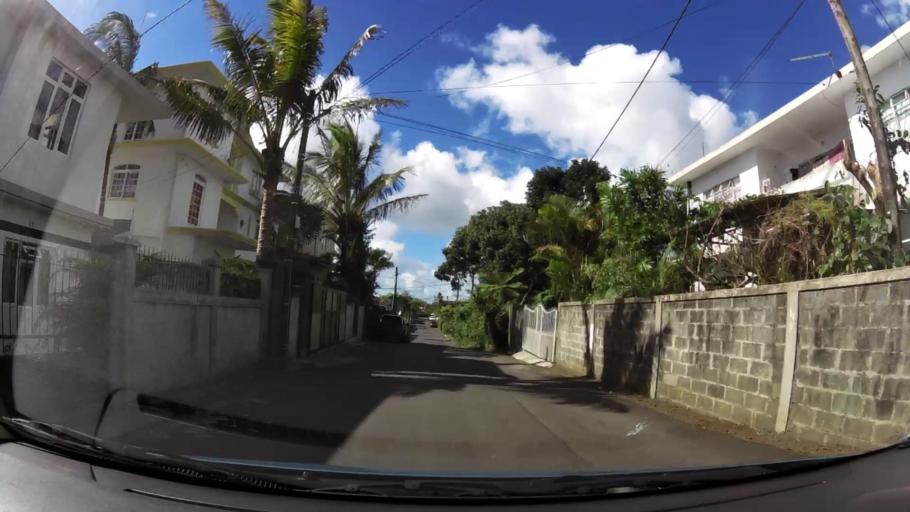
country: MU
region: Plaines Wilhems
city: Curepipe
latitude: -20.3288
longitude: 57.5194
